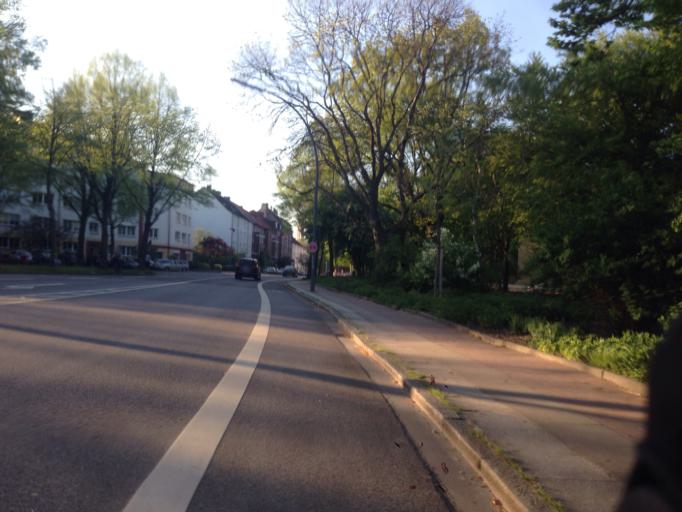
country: DE
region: Hamburg
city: Rothenburgsort
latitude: 53.5513
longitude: 10.0589
